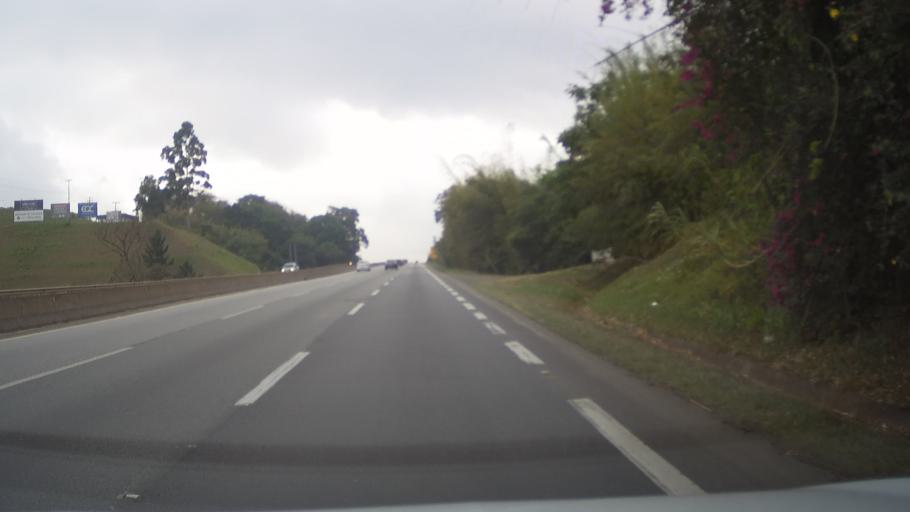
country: BR
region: Minas Gerais
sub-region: Extrema
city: Extrema
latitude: -22.8692
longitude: -46.3558
